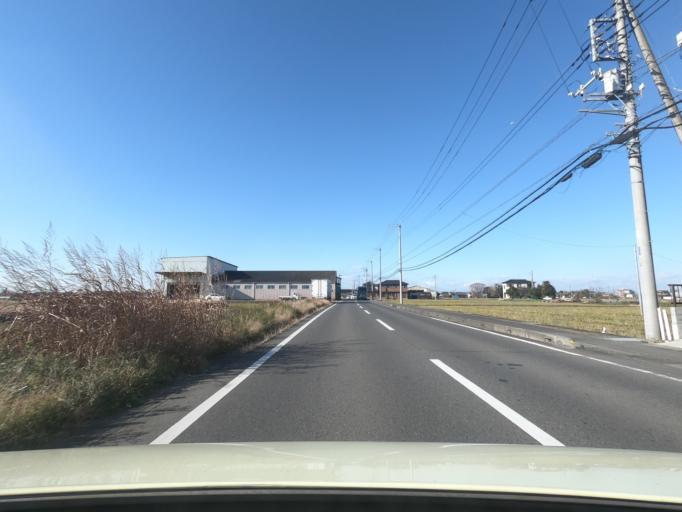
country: JP
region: Ibaraki
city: Ishige
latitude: 36.1768
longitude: 139.9768
